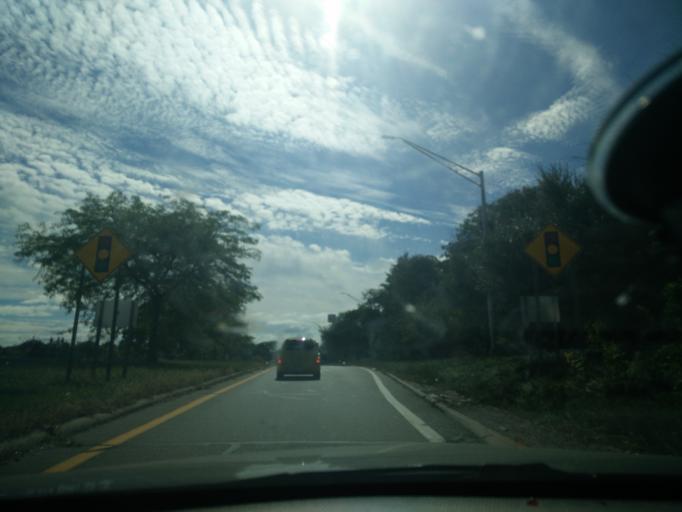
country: US
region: Michigan
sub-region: Macomb County
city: Roseville
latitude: 42.4822
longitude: -82.9174
